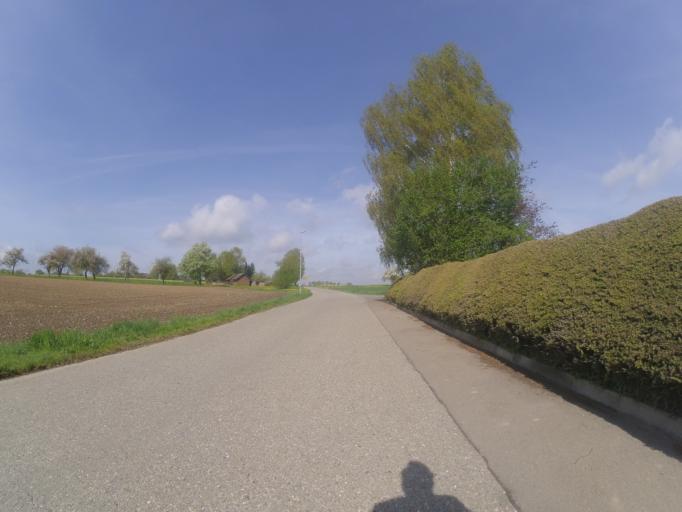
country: DE
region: Baden-Wuerttemberg
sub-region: Tuebingen Region
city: Griesingen
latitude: 48.2306
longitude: 9.8183
